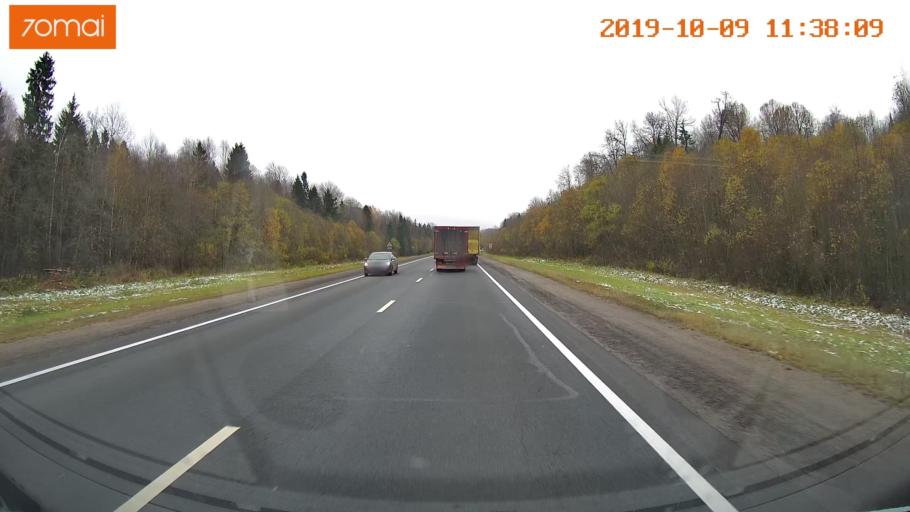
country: RU
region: Vologda
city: Gryazovets
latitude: 58.9712
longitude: 40.1532
